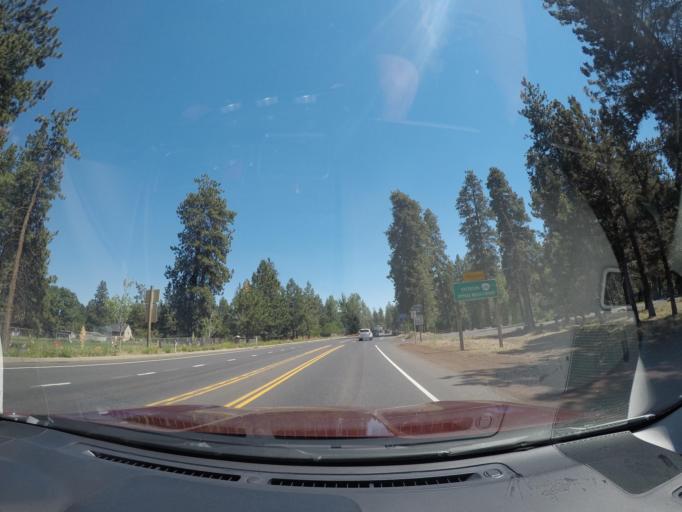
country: US
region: Oregon
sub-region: Deschutes County
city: Sisters
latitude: 44.2894
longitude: -121.5426
